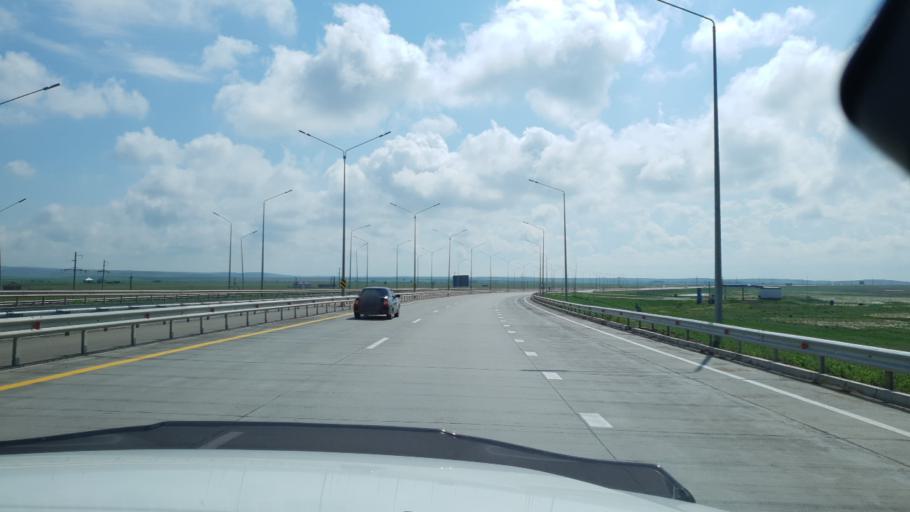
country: KZ
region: Qaraghandy
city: Osakarovka
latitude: 50.8115
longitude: 72.1865
